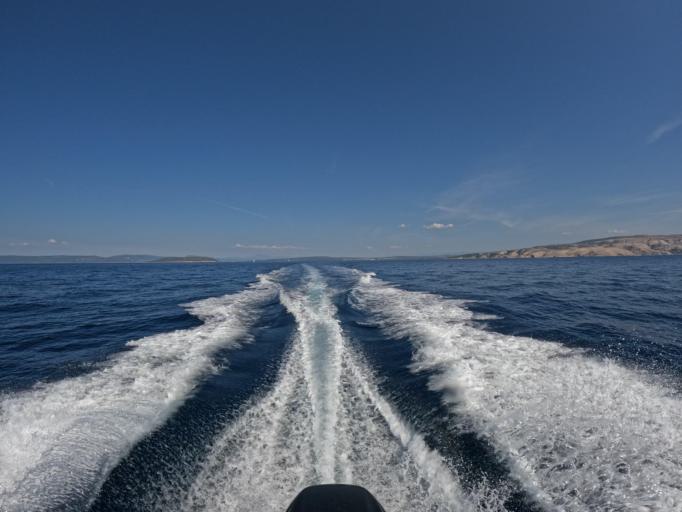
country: HR
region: Primorsko-Goranska
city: Punat
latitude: 44.9189
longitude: 14.6232
